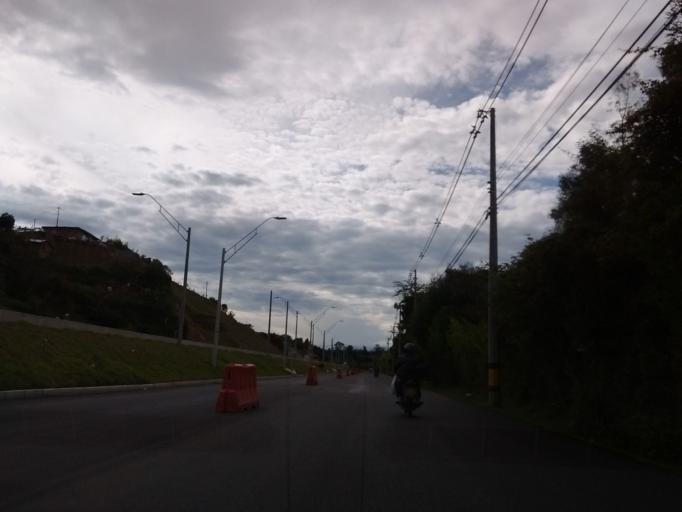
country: CO
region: Antioquia
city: Santuario
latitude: 6.1374
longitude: -75.2966
